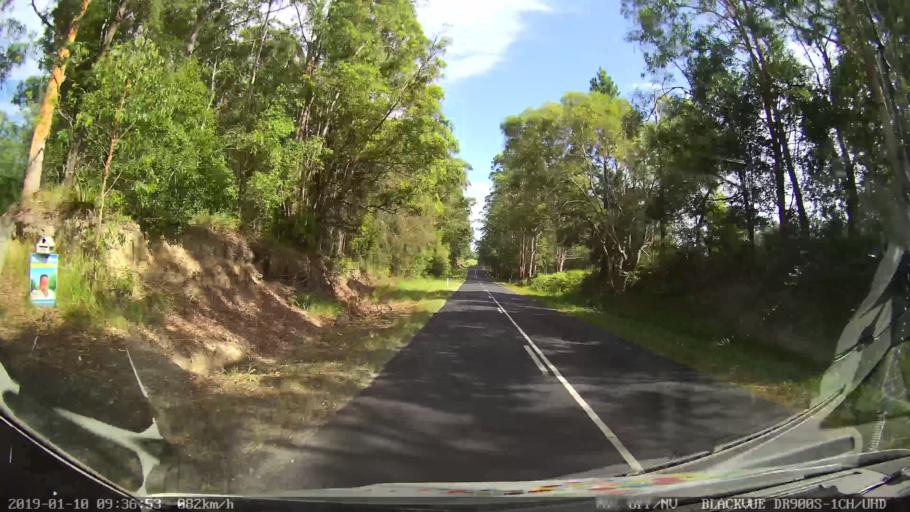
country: AU
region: New South Wales
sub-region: Coffs Harbour
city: Nana Glen
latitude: -30.1939
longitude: 153.0128
